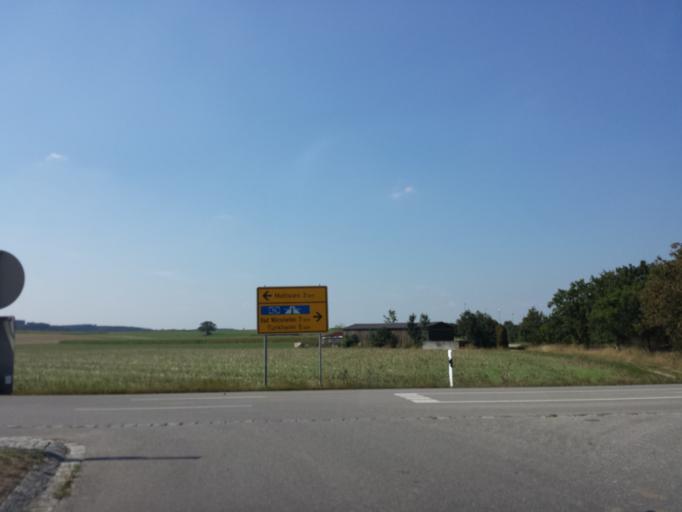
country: DE
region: Bavaria
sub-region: Swabia
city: Tussenhausen
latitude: 48.0728
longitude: 10.5755
